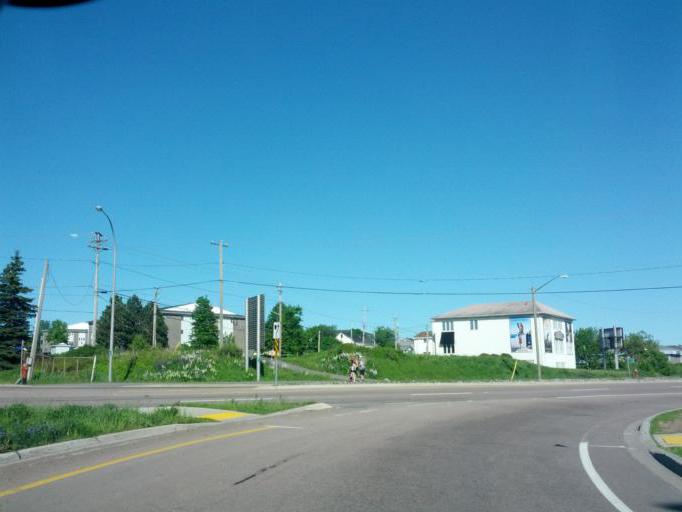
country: CA
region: New Brunswick
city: Moncton
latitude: 46.1002
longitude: -64.7628
